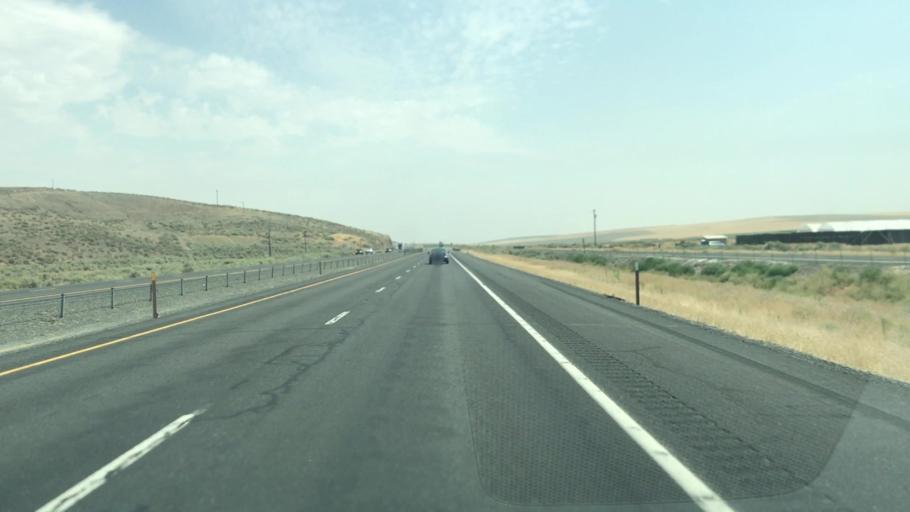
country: US
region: Washington
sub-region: Grant County
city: Warden
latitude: 47.0843
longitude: -118.9903
